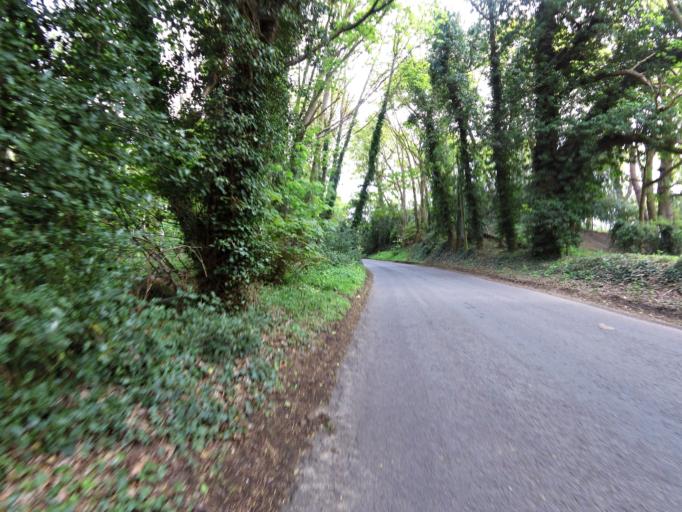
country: GB
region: England
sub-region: Suffolk
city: Ipswich
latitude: 51.9802
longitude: 1.1645
